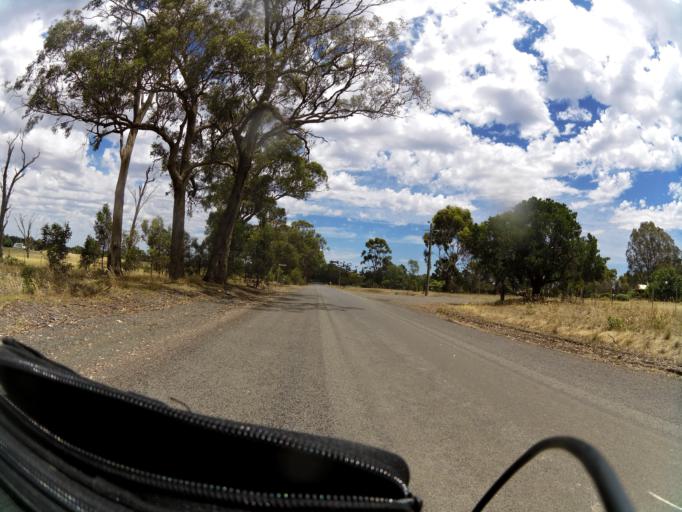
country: AU
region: Victoria
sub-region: Campaspe
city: Kyabram
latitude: -36.7388
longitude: 145.1390
